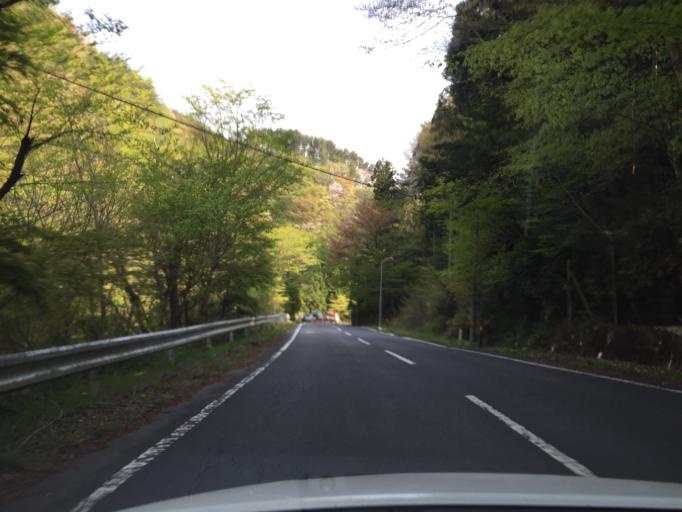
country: JP
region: Fukushima
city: Iwaki
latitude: 37.1751
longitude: 140.8508
